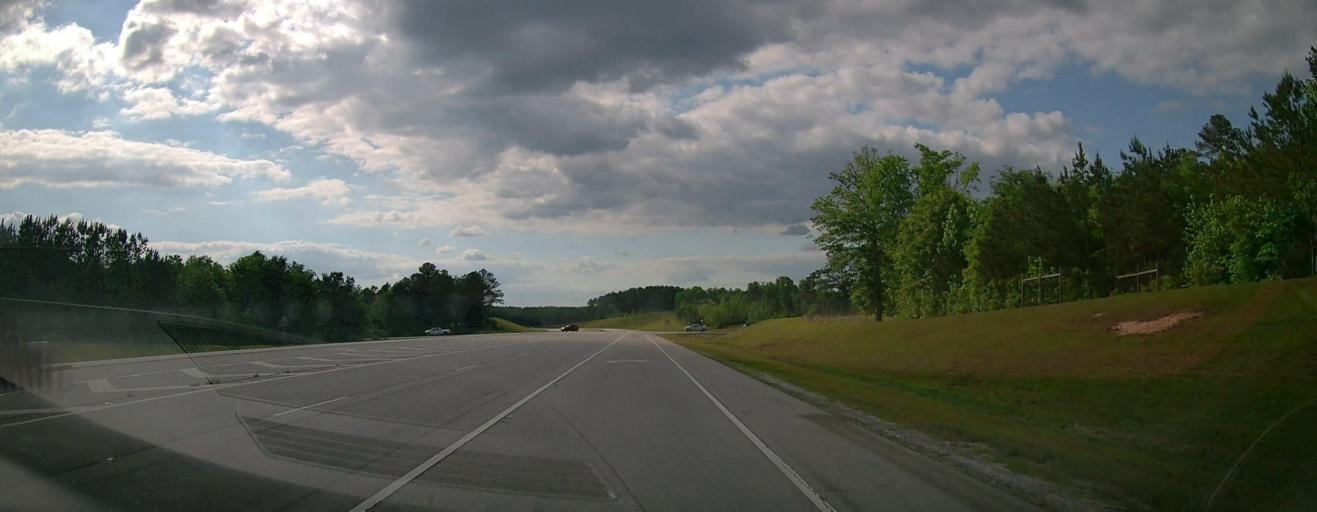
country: US
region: Georgia
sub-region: Baldwin County
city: Hardwick
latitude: 33.0372
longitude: -83.1145
